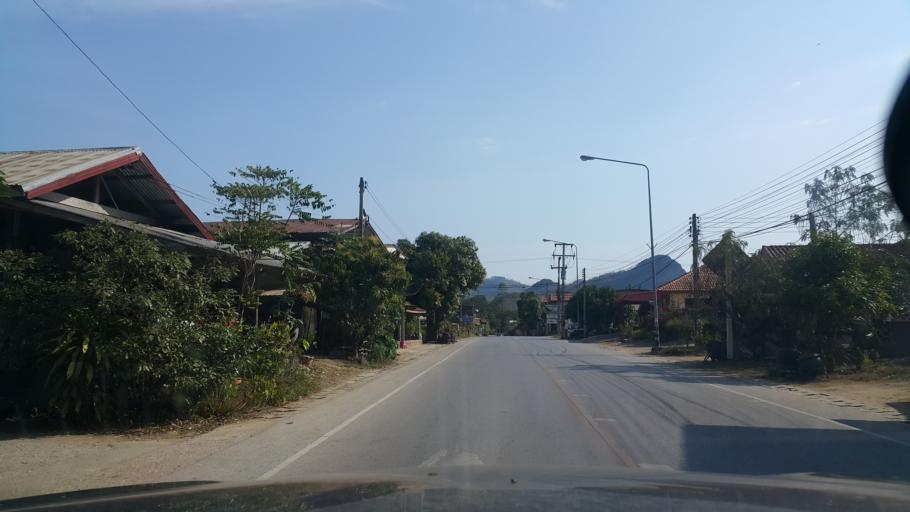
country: LA
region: Vientiane
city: Muang Sanakham
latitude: 17.9067
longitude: 101.7256
